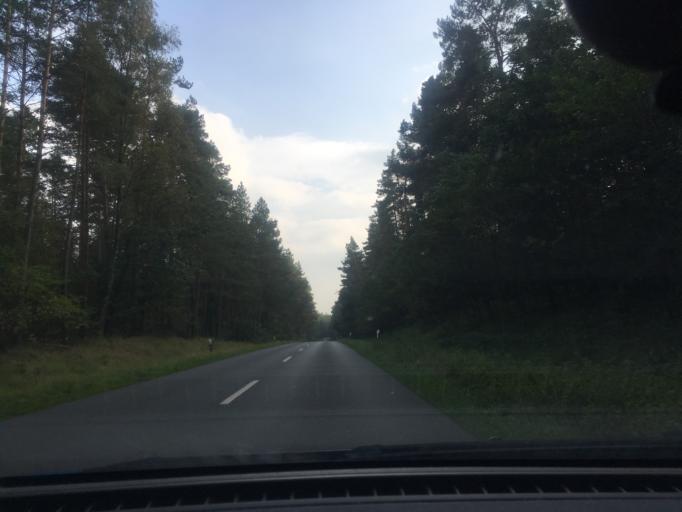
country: DE
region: Lower Saxony
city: Barendorf
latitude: 53.2517
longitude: 10.5279
